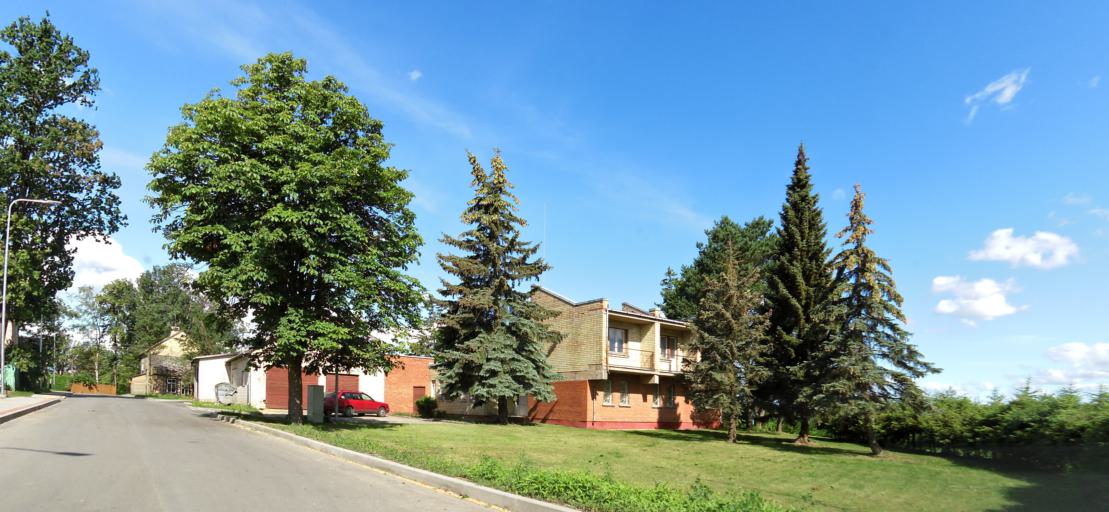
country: LT
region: Panevezys
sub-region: Birzai
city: Birzai
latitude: 56.2029
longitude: 24.7488
